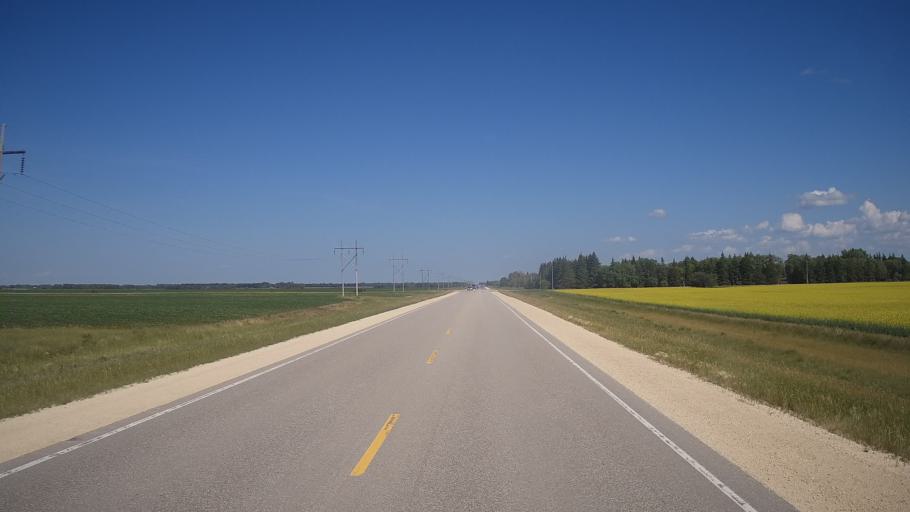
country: CA
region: Manitoba
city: Stonewall
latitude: 50.1227
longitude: -97.3949
